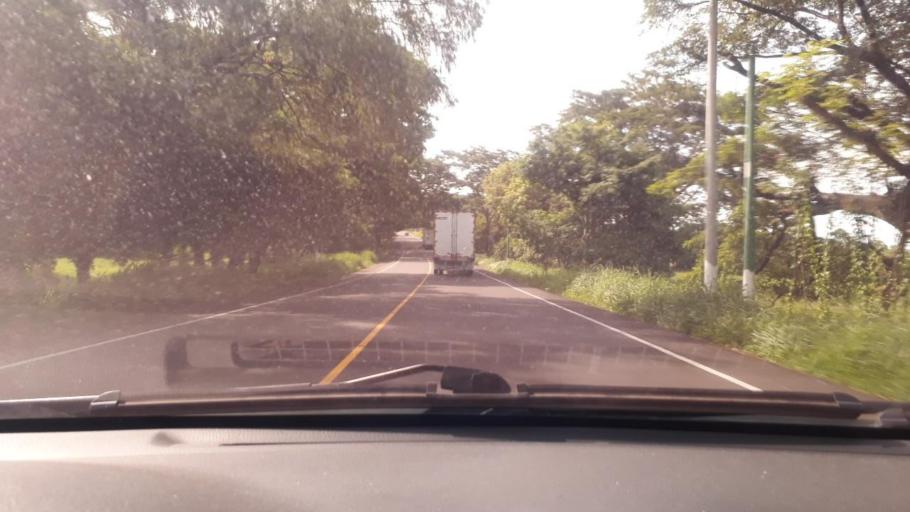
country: GT
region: Jutiapa
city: Pasaco
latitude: 13.8820
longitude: -90.1340
